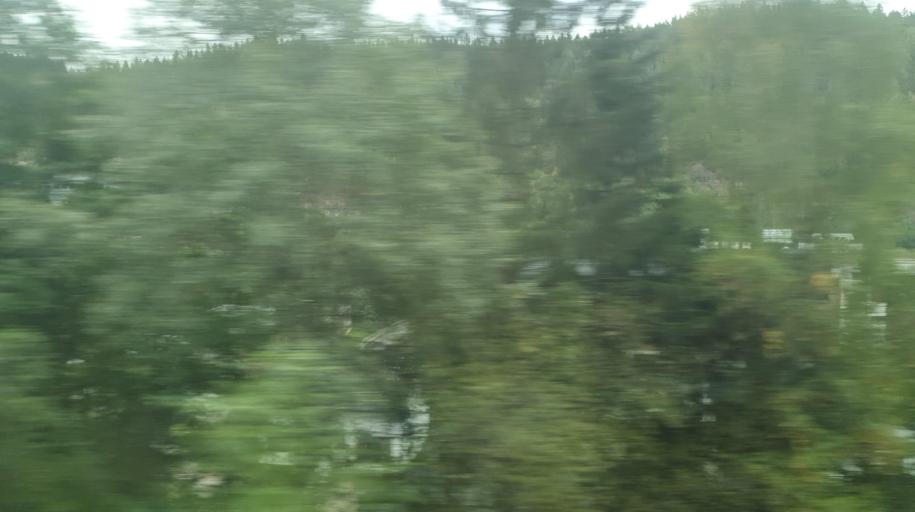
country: NO
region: Buskerud
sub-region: Drammen
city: Skoger
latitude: 59.7084
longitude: 10.2356
